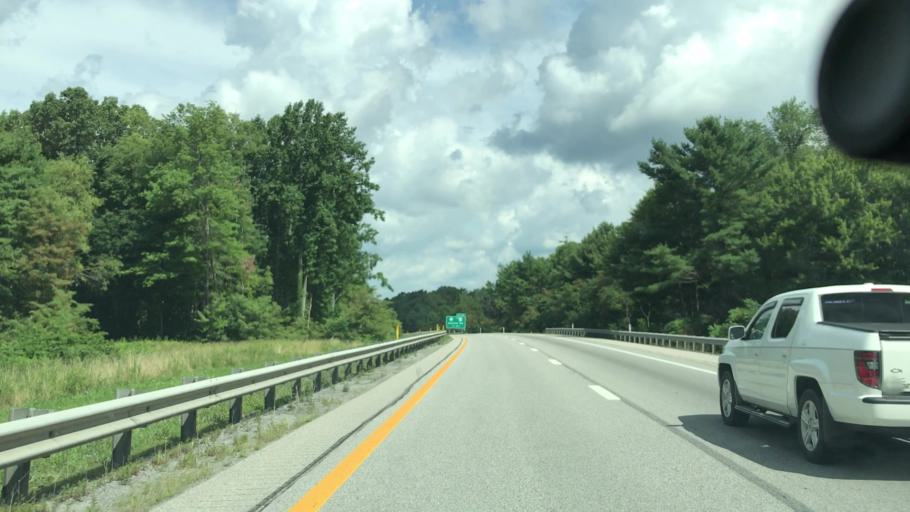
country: US
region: West Virginia
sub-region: Mercer County
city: Athens
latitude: 37.4121
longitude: -81.0616
